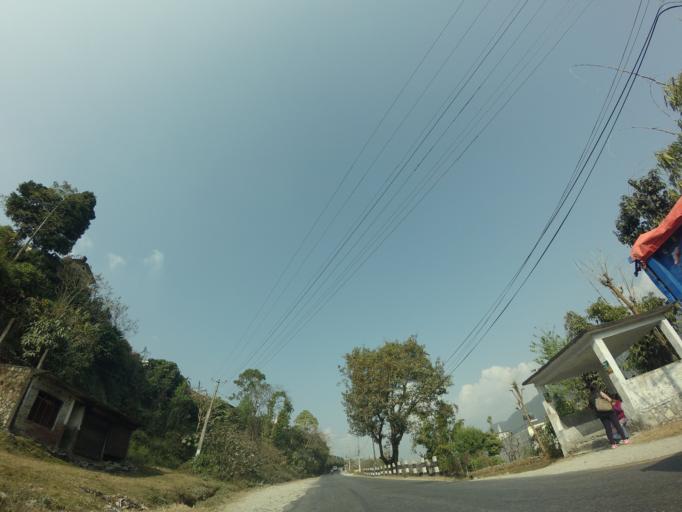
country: NP
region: Western Region
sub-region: Gandaki Zone
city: Pokhara
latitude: 28.2610
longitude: 83.9589
